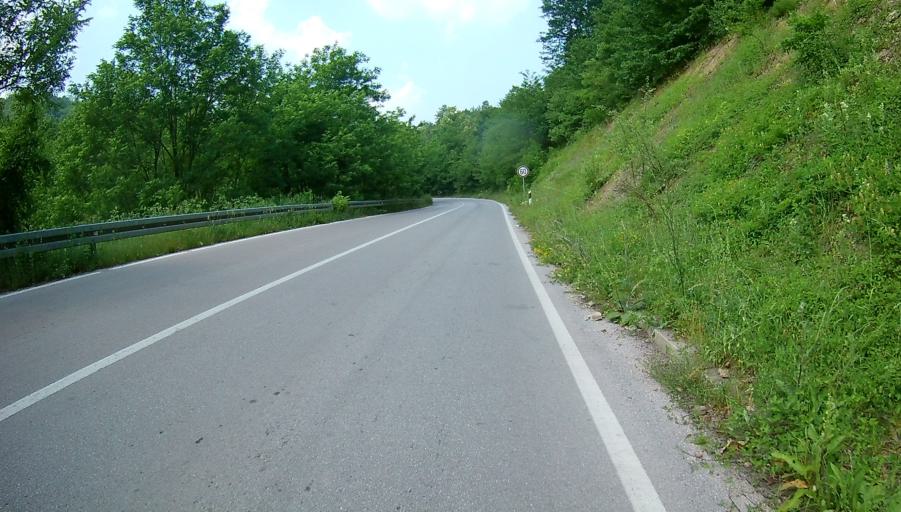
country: RS
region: Central Serbia
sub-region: Nisavski Okrug
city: Gadzin Han
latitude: 43.1815
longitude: 22.0444
